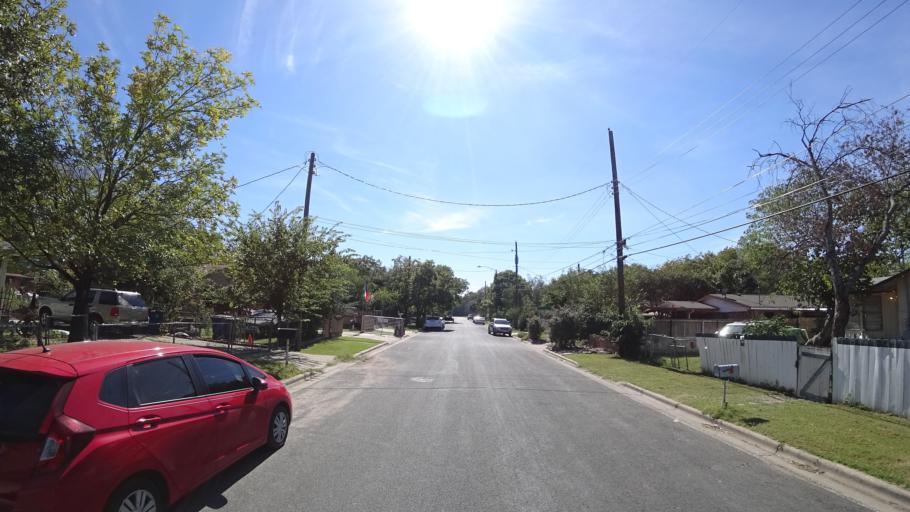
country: US
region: Texas
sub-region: Travis County
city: Austin
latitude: 30.2688
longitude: -97.6819
